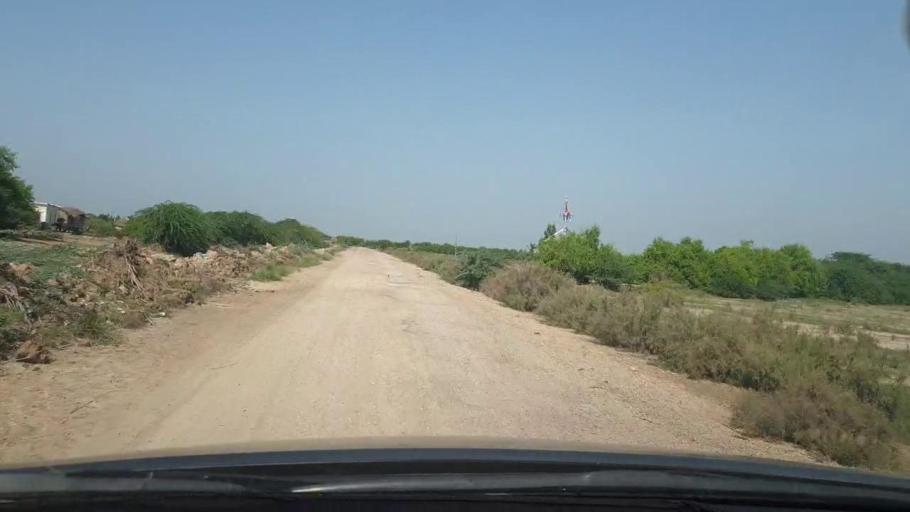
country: PK
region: Sindh
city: Tando Bago
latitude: 24.7179
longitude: 69.1032
